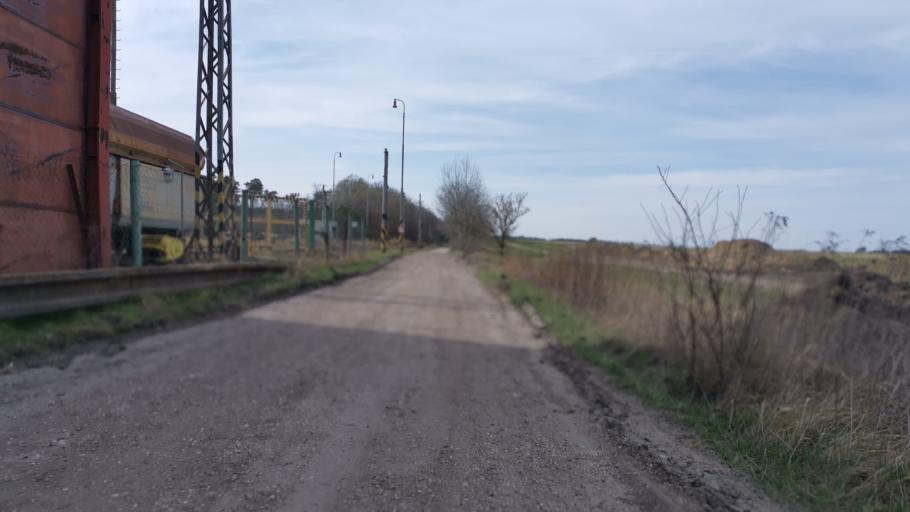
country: SK
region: Trnavsky
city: Gbely
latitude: 48.6606
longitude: 17.0745
